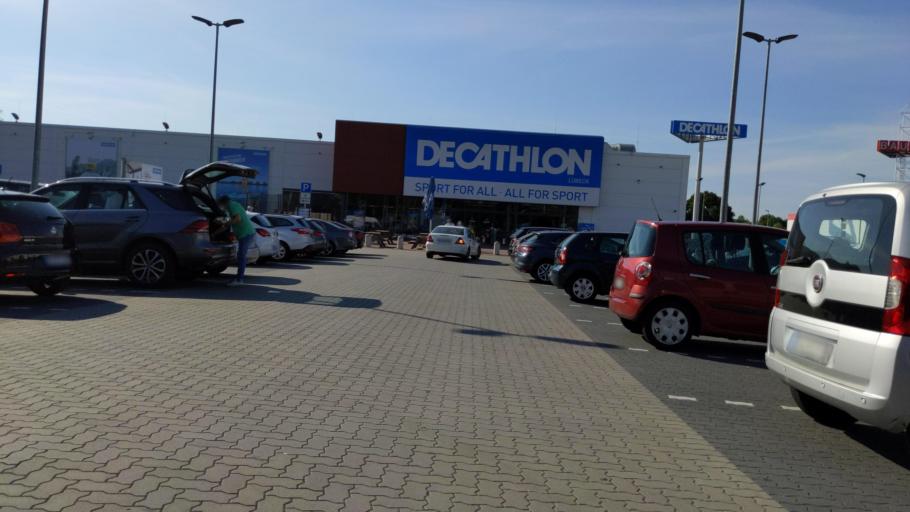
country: DE
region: Schleswig-Holstein
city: Stockelsdorf
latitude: 53.8614
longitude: 10.6277
